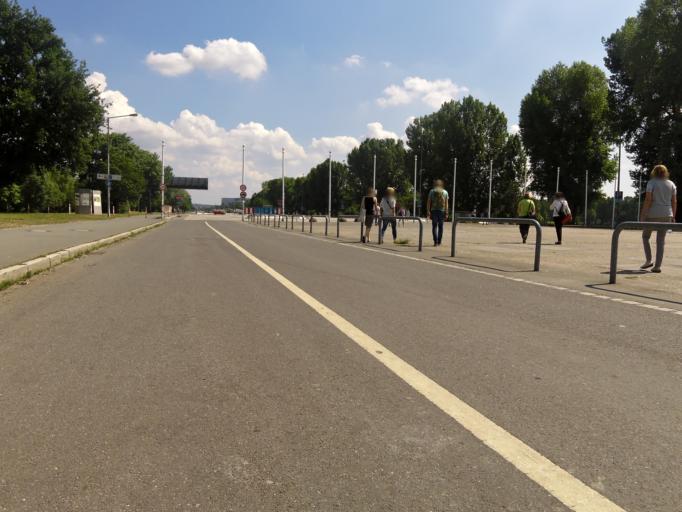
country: DE
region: Bavaria
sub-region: Regierungsbezirk Mittelfranken
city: Nuernberg
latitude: 49.4290
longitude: 11.1119
